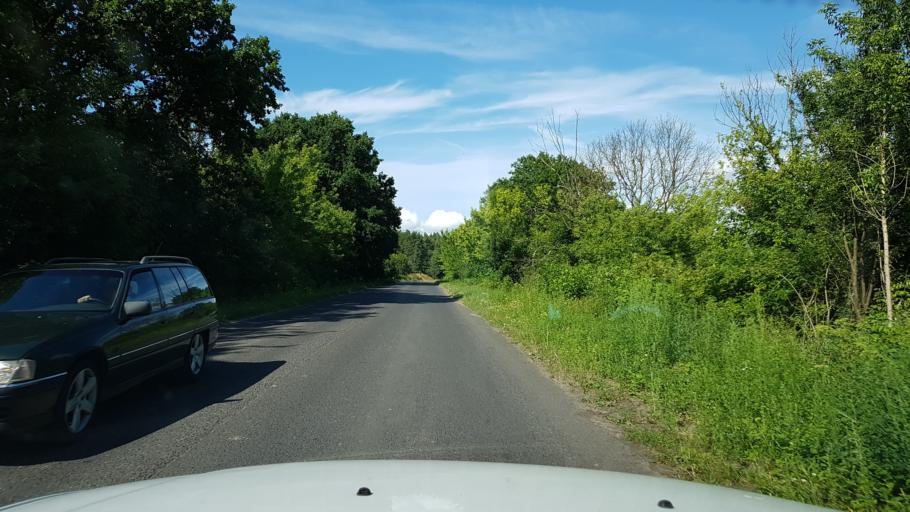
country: PL
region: West Pomeranian Voivodeship
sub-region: Powiat gryfinski
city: Stare Czarnowo
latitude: 53.2929
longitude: 14.7857
